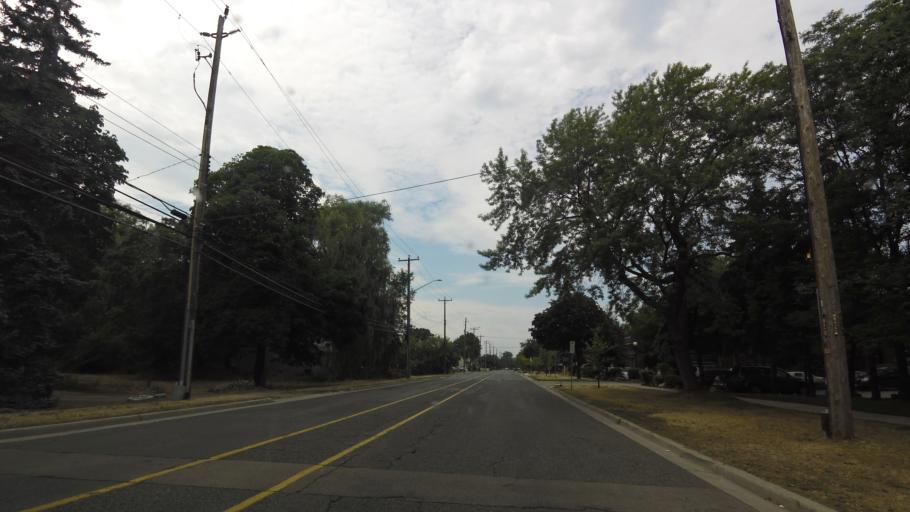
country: CA
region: Ontario
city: Hamilton
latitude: 43.2760
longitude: -79.7814
